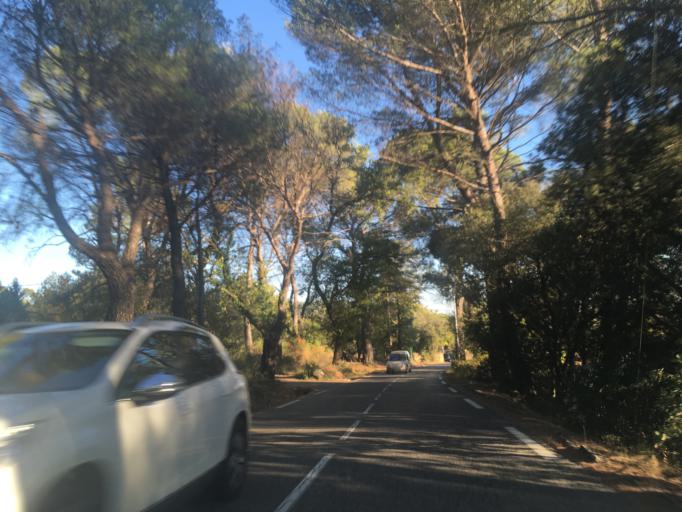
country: FR
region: Provence-Alpes-Cote d'Azur
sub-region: Departement du Var
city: Villecroze
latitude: 43.5724
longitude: 6.2855
